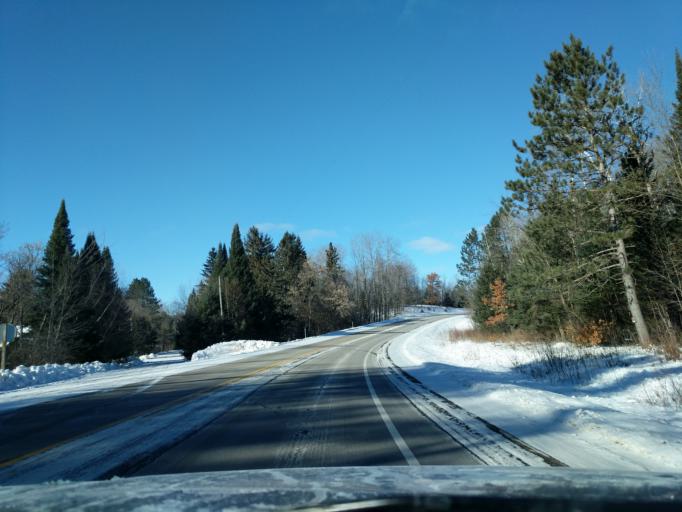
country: US
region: Wisconsin
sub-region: Menominee County
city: Keshena
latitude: 45.1196
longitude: -88.6628
